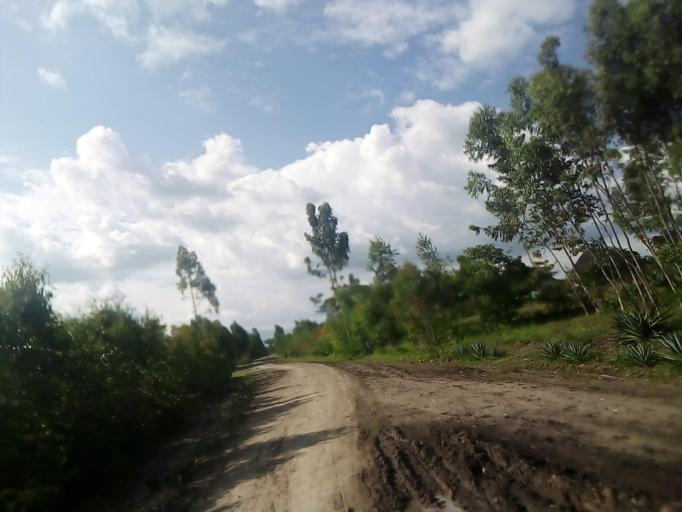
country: ET
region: Southern Nations, Nationalities, and People's Region
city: K'olito
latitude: 7.6524
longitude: 38.0503
